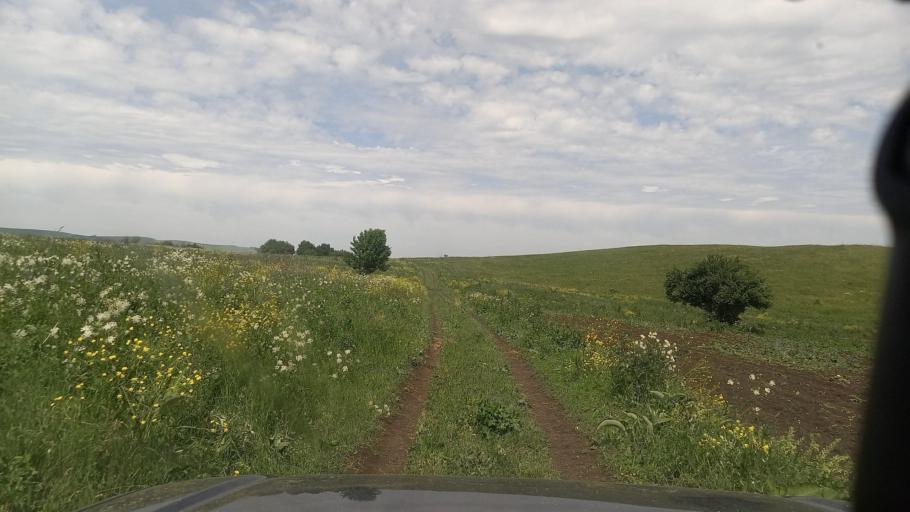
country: RU
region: Krasnodarskiy
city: Peredovaya
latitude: 44.0704
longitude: 41.3175
